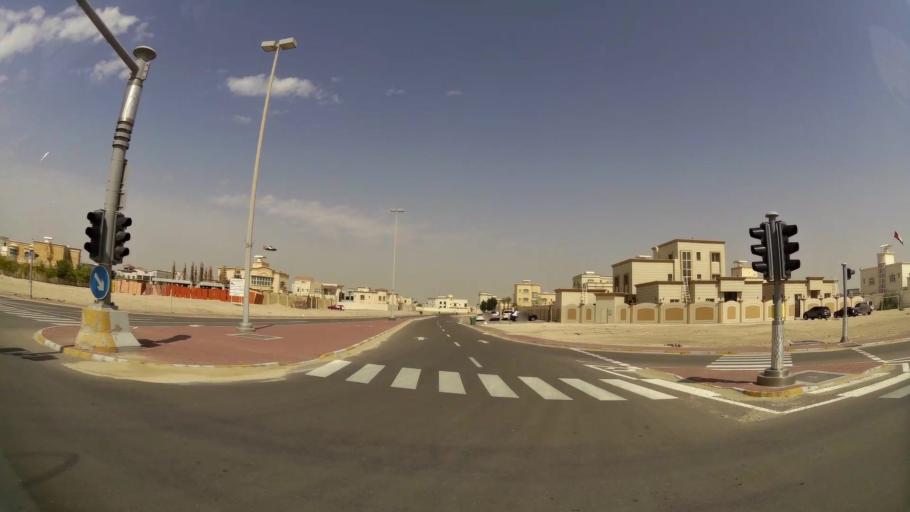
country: AE
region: Abu Dhabi
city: Abu Dhabi
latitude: 24.3067
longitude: 54.5503
